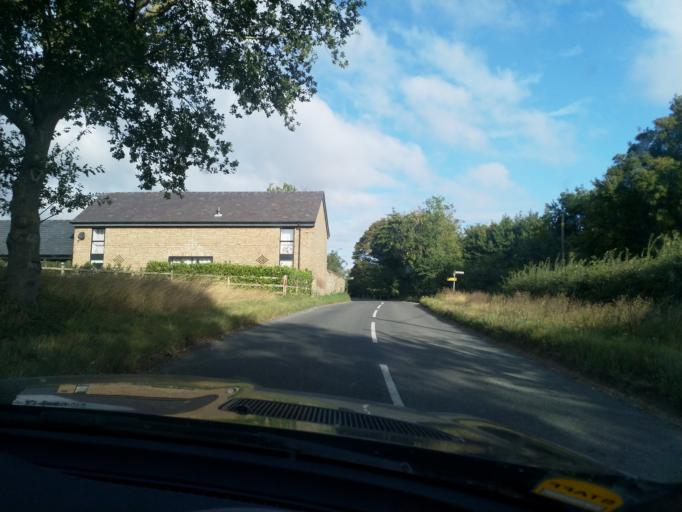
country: GB
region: England
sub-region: Suffolk
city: Elmswell
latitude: 52.2292
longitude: 0.9311
